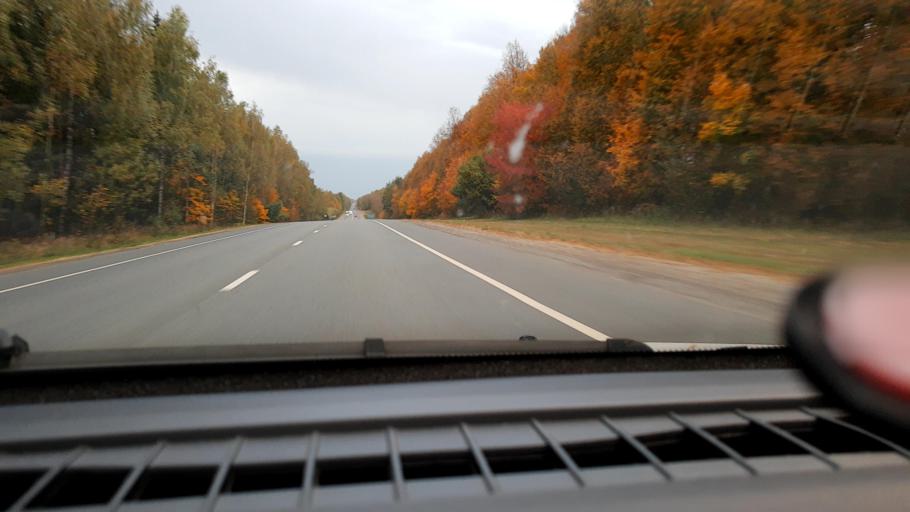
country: RU
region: Vladimir
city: Orgtrud
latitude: 56.2003
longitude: 40.8098
